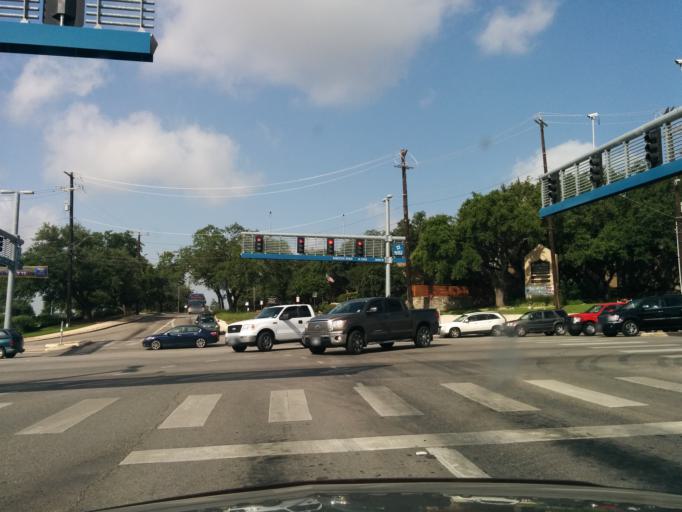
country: US
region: Texas
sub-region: Bexar County
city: Leon Valley
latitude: 29.5091
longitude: -98.5896
